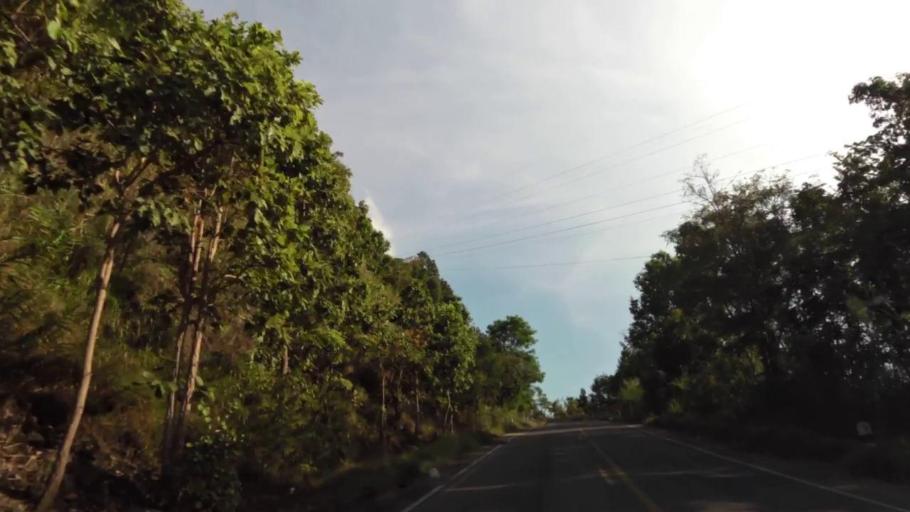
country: TH
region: Chiang Rai
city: Khun Tan
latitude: 19.8775
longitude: 100.3144
